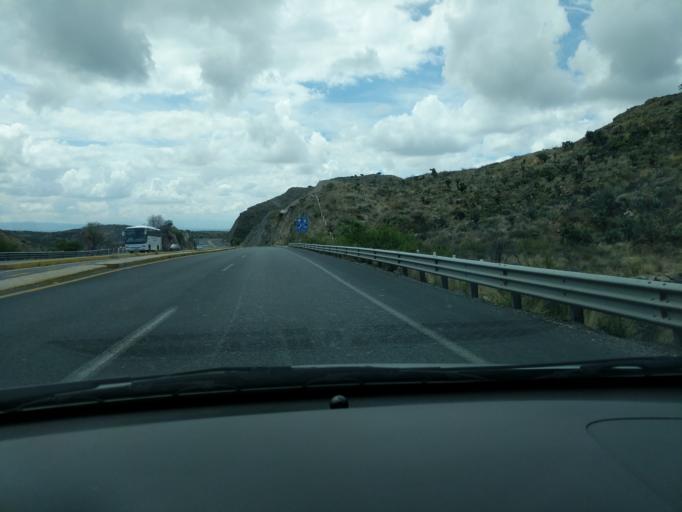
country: MX
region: San Luis Potosi
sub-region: Mexquitic de Carmona
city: Cerrito de Jaral
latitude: 22.2489
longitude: -101.1048
